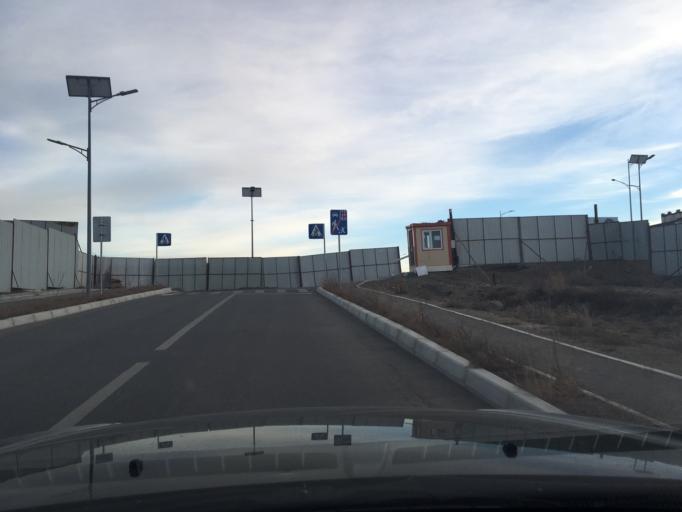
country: MN
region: Ulaanbaatar
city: Ulaanbaatar
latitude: 47.8472
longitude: 106.7909
